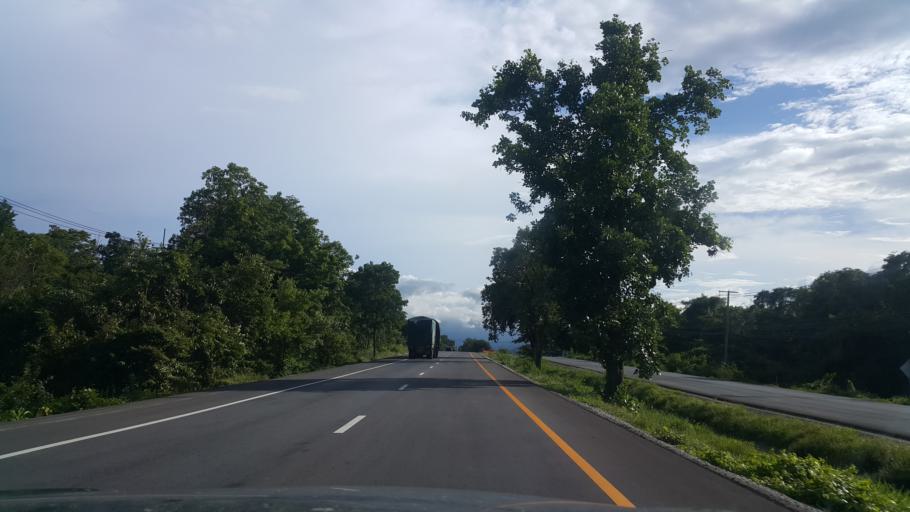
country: TH
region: Tak
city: Ban Tak
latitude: 17.1322
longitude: 99.1043
